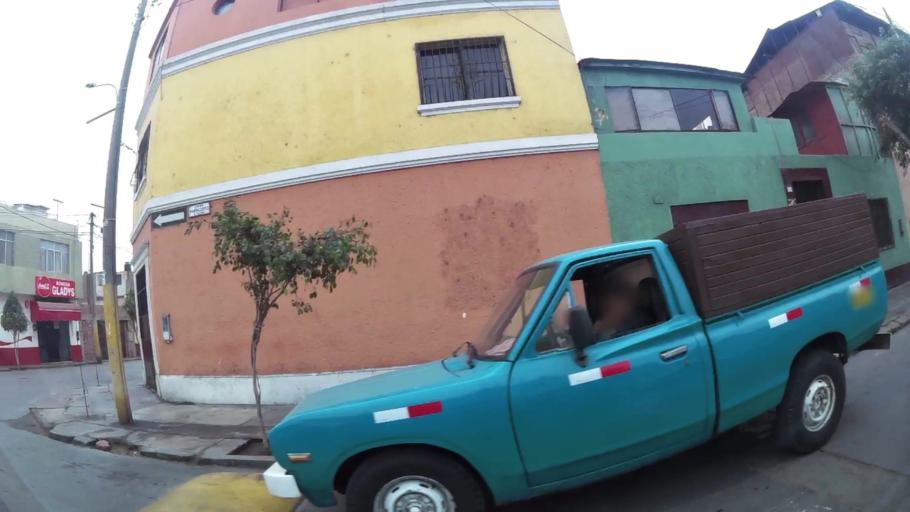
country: PE
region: Lima
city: Lima
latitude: -12.0523
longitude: -77.0520
